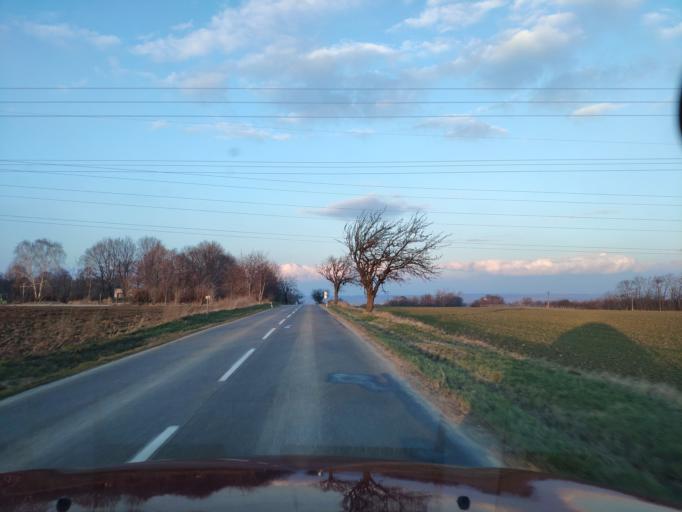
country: SK
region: Nitriansky
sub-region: Okres Nitra
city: Nitra
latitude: 48.2268
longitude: 18.0994
